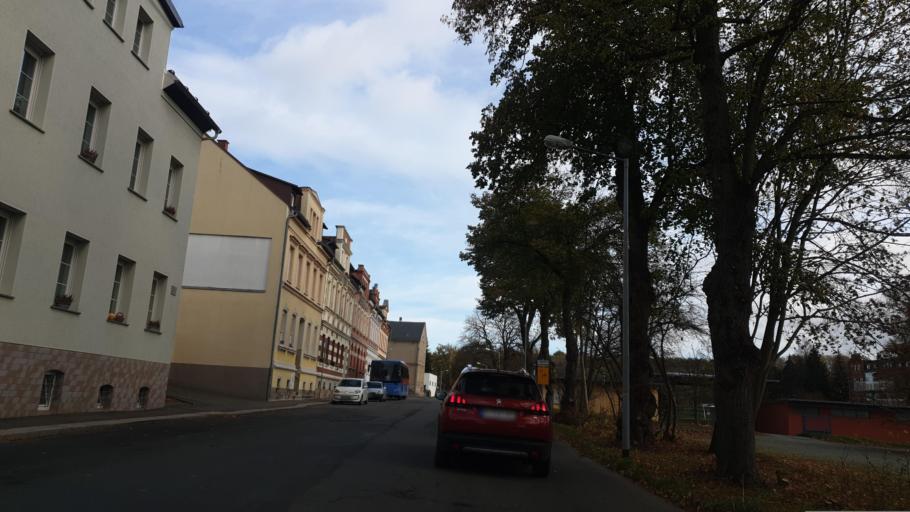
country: DE
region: Saxony
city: Reichenbach/Vogtland
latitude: 50.6330
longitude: 12.3272
